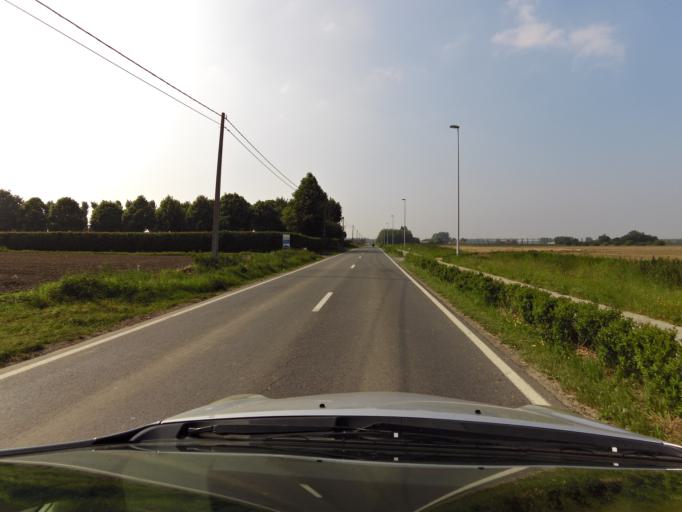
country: BE
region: Flanders
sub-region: Provincie West-Vlaanderen
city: Poperinge
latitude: 50.8682
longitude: 2.7140
